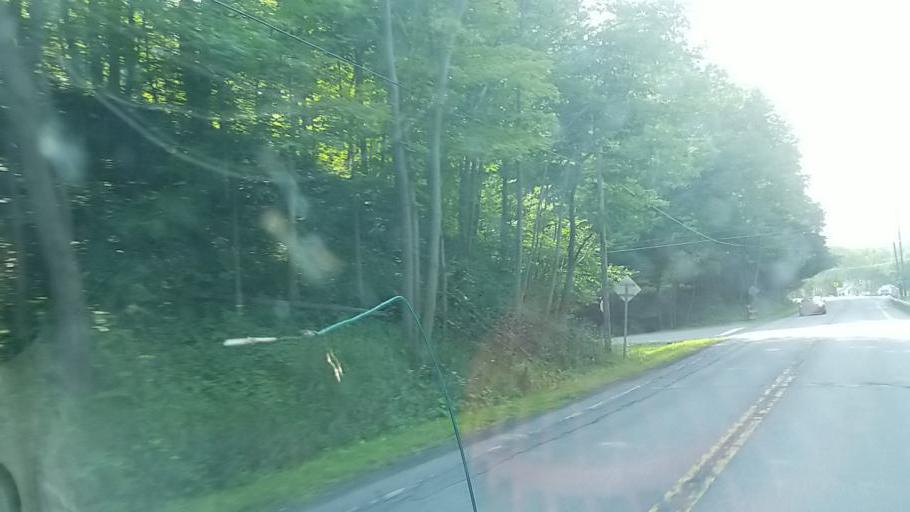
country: US
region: New York
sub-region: Montgomery County
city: Tribes Hill
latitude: 42.9380
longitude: -74.2725
